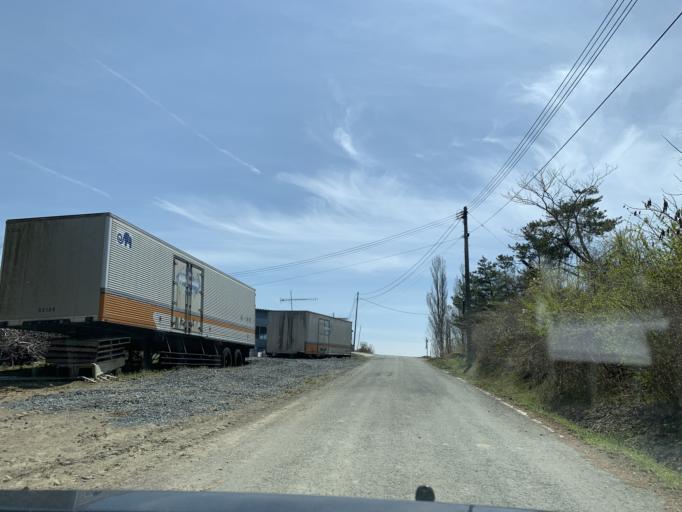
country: JP
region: Iwate
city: Ichinoseki
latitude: 38.8103
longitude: 141.2722
